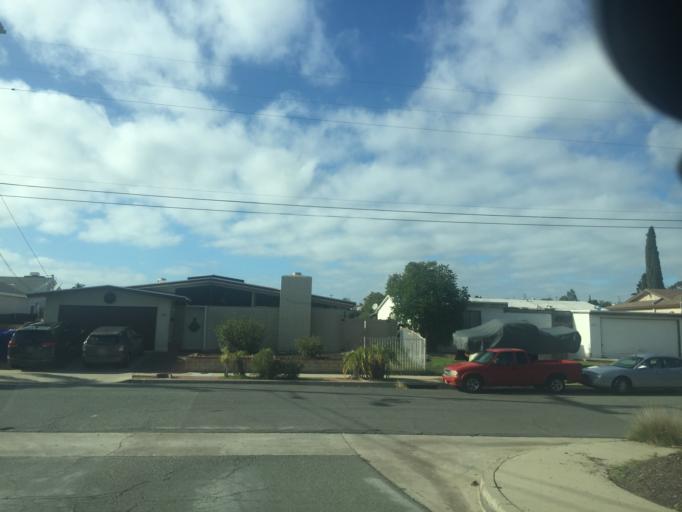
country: US
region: California
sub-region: San Diego County
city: San Diego
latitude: 32.7854
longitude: -117.1512
